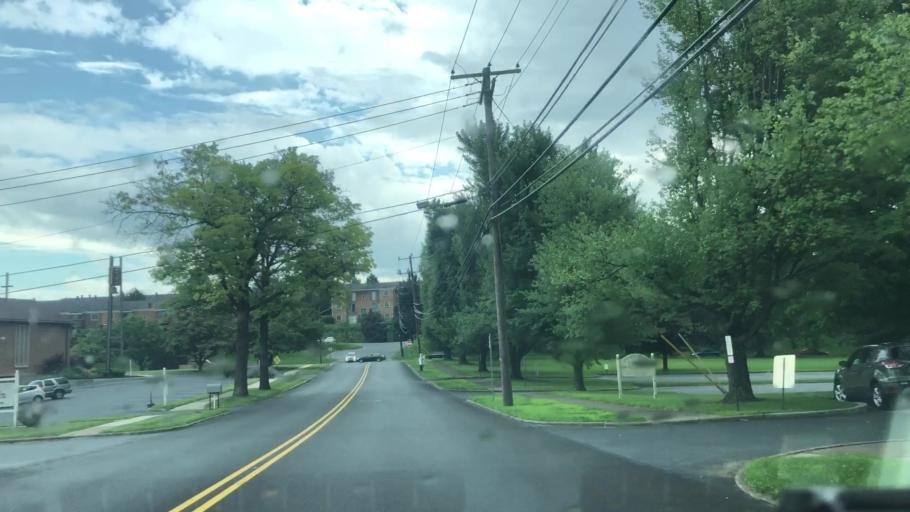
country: US
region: Pennsylvania
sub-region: Dauphin County
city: Progress
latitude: 40.2833
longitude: -76.8191
